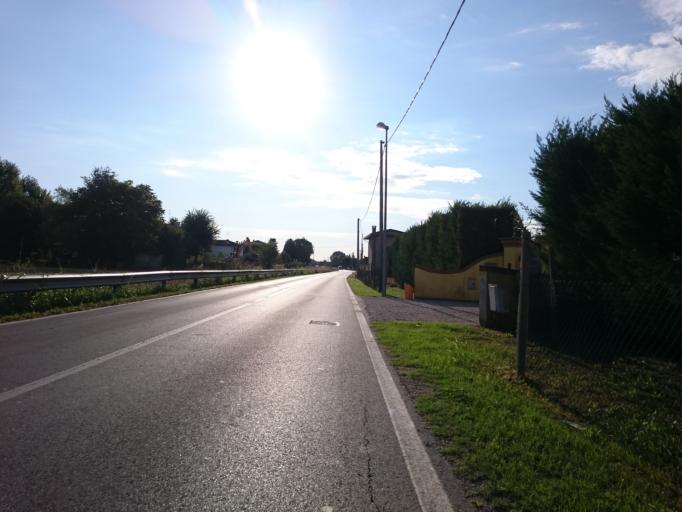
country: IT
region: Veneto
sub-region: Provincia di Padova
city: Masera di Padova
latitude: 45.3282
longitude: 11.8460
